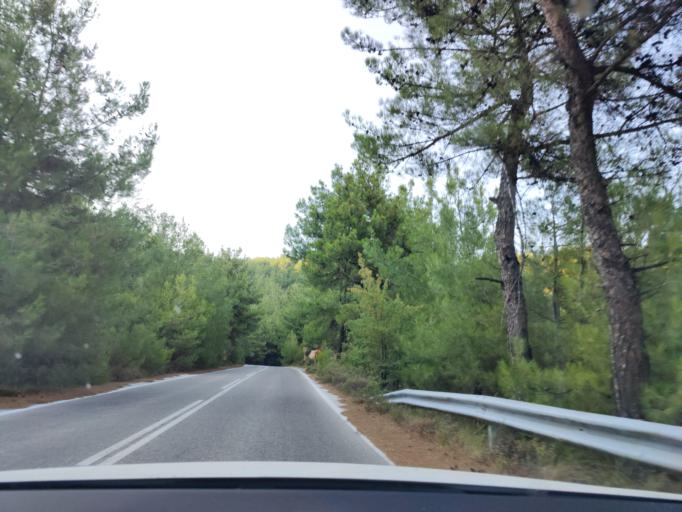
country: GR
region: East Macedonia and Thrace
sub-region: Nomos Kavalas
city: Potamia
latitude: 40.6268
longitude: 24.7645
